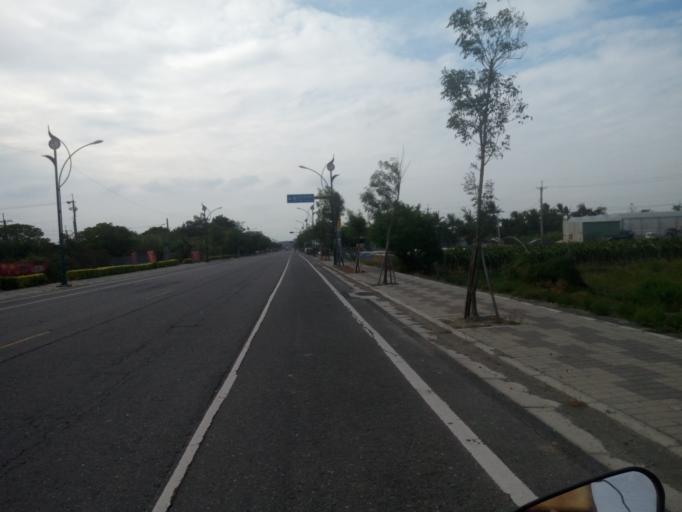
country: TW
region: Taiwan
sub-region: Chiayi
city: Taibao
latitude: 23.4920
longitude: 120.3434
